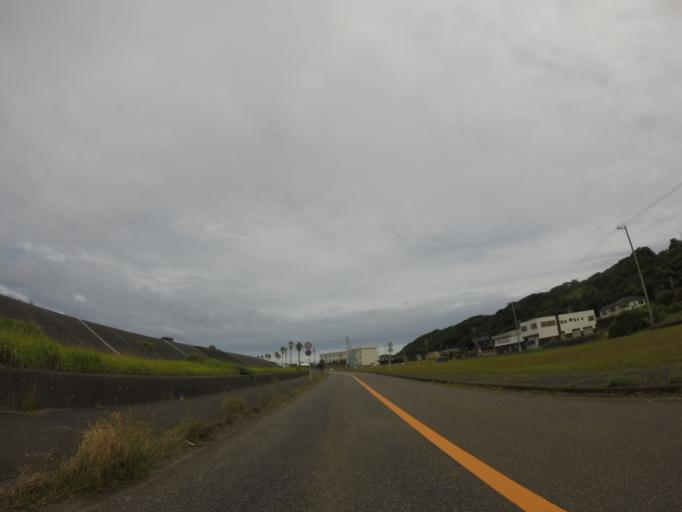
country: JP
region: Shizuoka
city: Oyama
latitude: 34.6043
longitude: 138.2274
